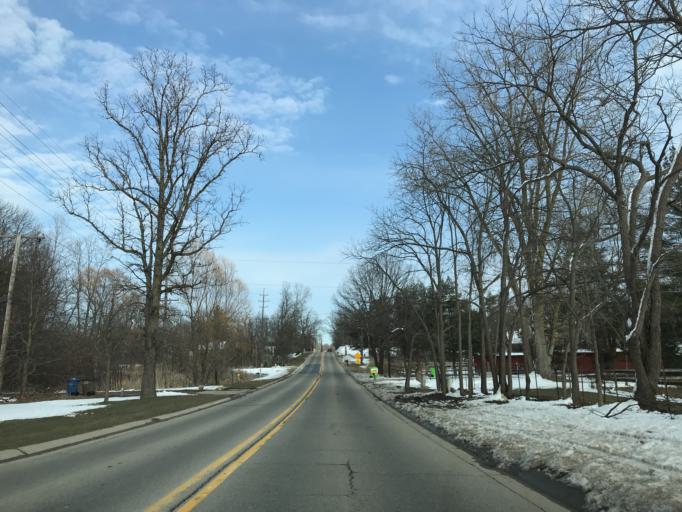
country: US
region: Michigan
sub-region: Oakland County
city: South Lyon
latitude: 42.4467
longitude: -83.6389
